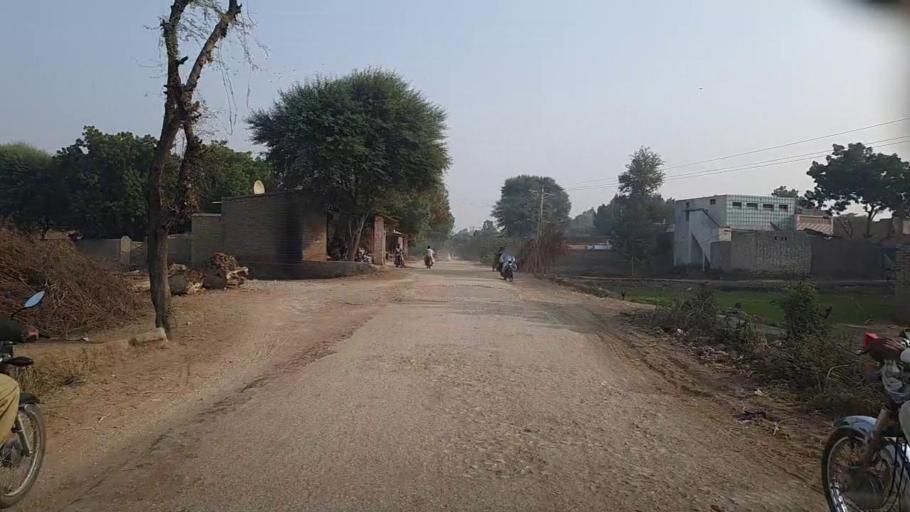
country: PK
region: Sindh
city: Kandiari
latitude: 27.0336
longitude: 68.4845
